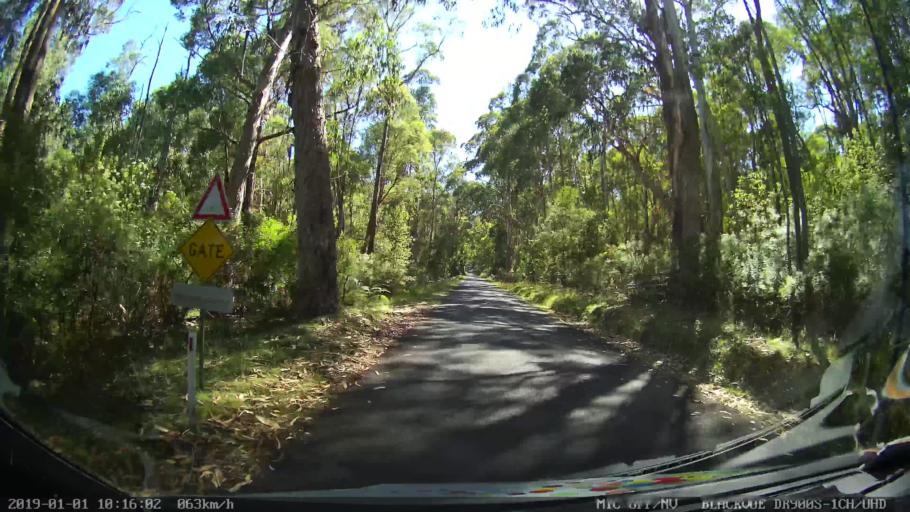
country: AU
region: New South Wales
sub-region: Snowy River
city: Jindabyne
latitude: -36.0963
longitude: 148.1639
